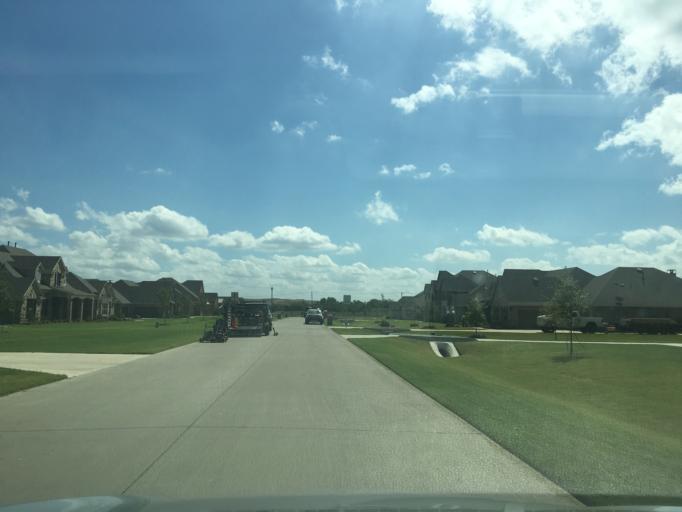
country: US
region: Texas
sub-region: Dallas County
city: Sachse
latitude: 32.9653
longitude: -96.5594
